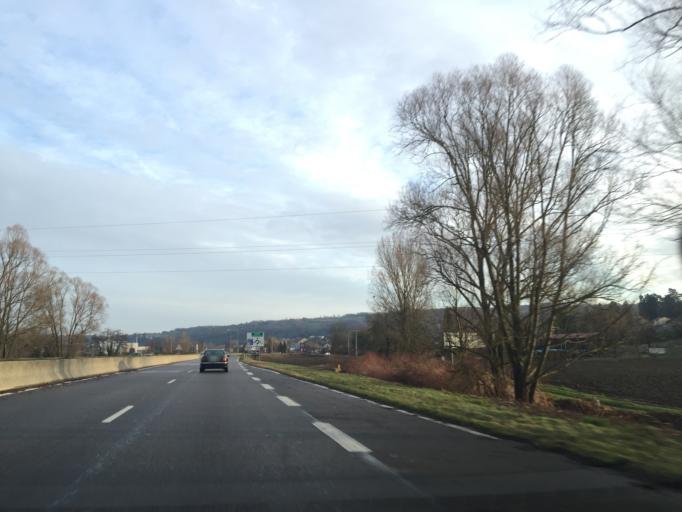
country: FR
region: Rhone-Alpes
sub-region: Departement de l'Isere
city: Saint-Alban-de-Roche
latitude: 45.6057
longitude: 5.2304
